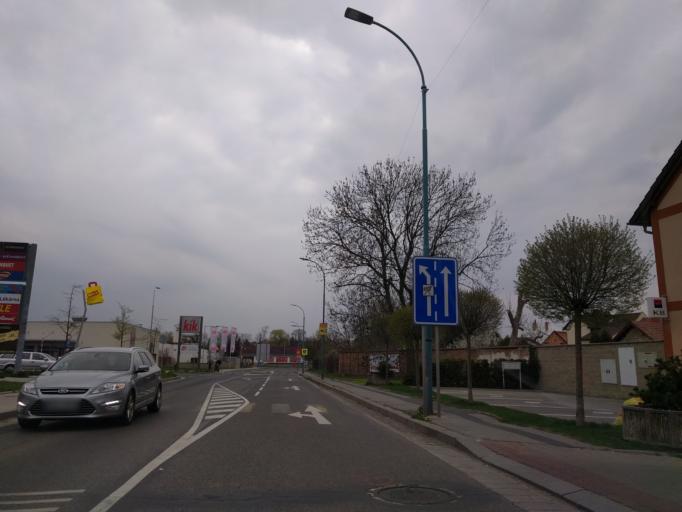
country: CZ
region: Central Bohemia
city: Cesky Brod
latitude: 50.0750
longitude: 14.8633
